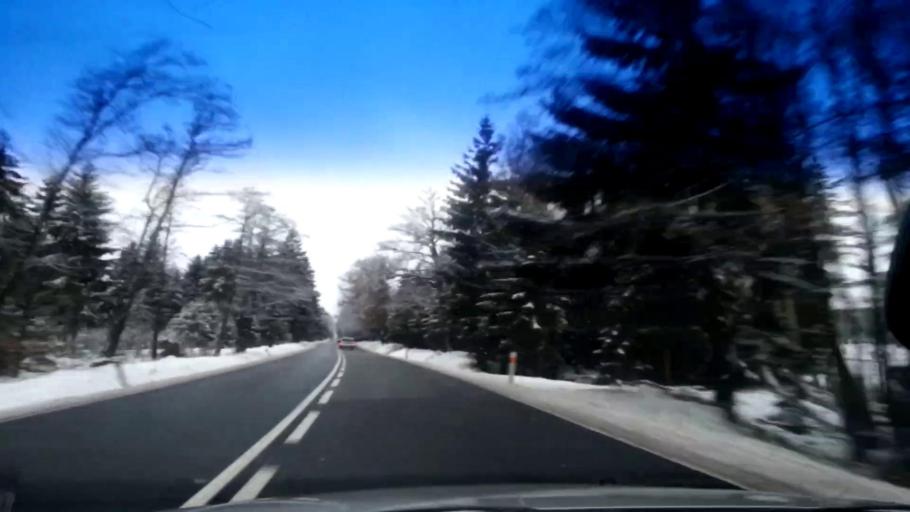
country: CZ
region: Karlovarsky
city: Hazlov
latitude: 50.1885
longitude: 12.2380
